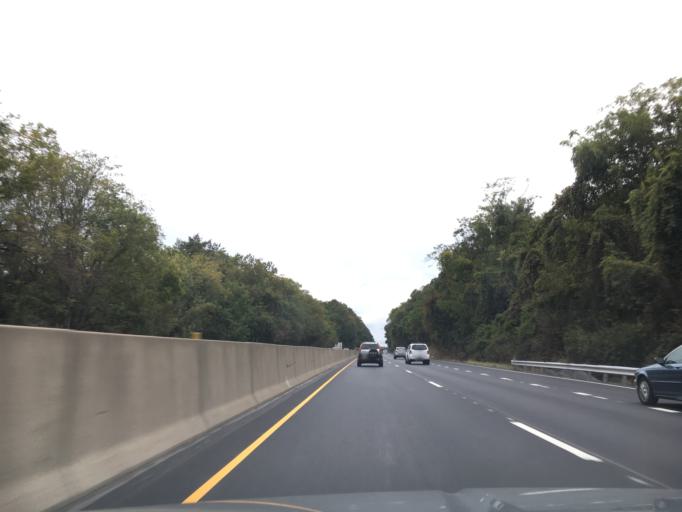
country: US
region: Pennsylvania
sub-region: Chester County
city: Thorndale
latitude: 40.0075
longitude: -75.7491
